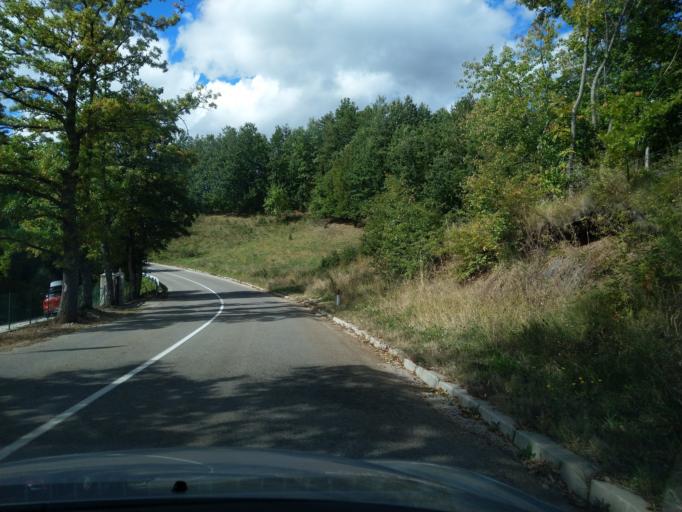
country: RS
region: Central Serbia
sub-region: Zlatiborski Okrug
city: Cajetina
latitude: 43.7223
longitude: 19.8159
